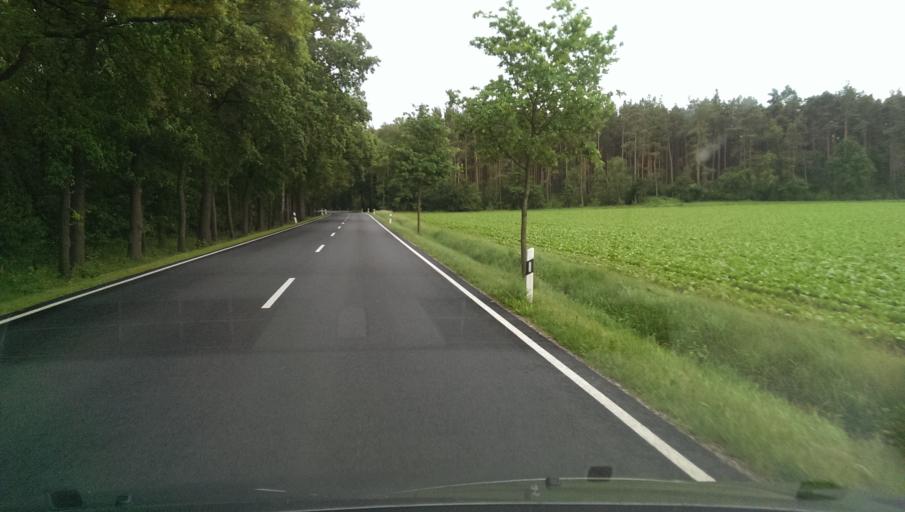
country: DE
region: Lower Saxony
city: Tulau
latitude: 52.6316
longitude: 10.8787
